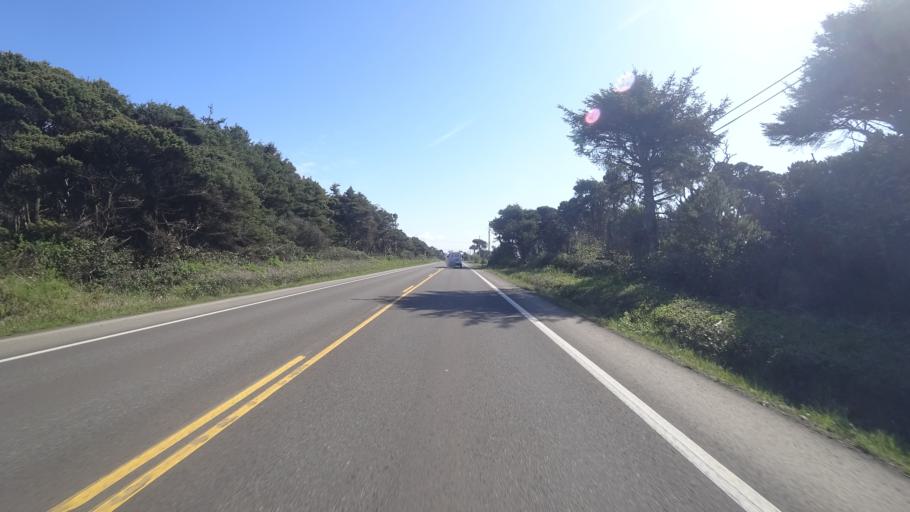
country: US
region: Oregon
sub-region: Lincoln County
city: Newport
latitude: 44.5361
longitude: -124.0744
